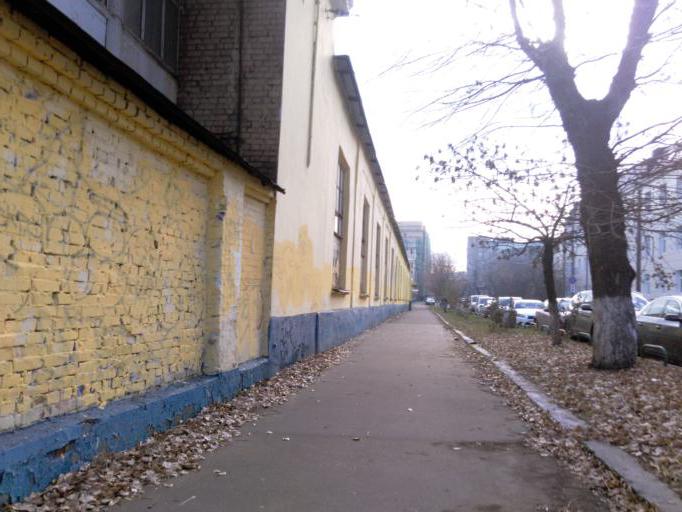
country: RU
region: Moscow
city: Mar'ina Roshcha
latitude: 55.8031
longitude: 37.5848
